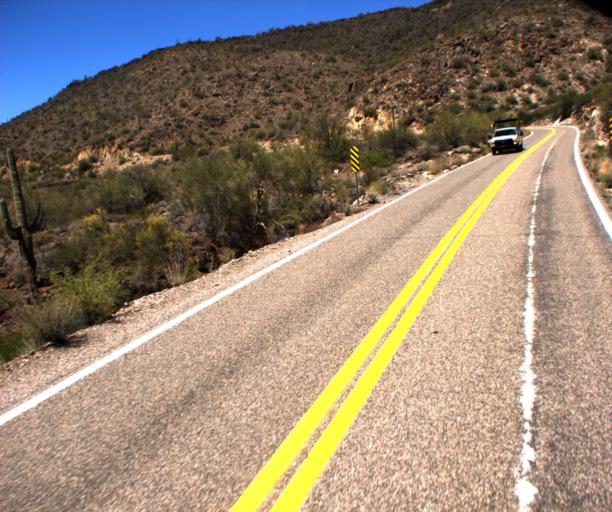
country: US
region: Arizona
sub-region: Yavapai County
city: Bagdad
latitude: 34.5034
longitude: -113.0688
